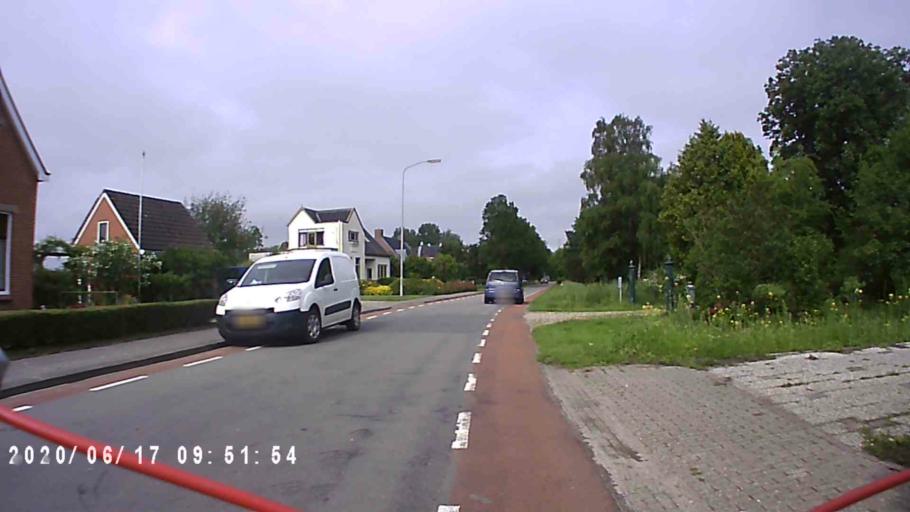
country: NL
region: Groningen
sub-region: Gemeente De Marne
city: Ulrum
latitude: 53.3598
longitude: 6.3272
